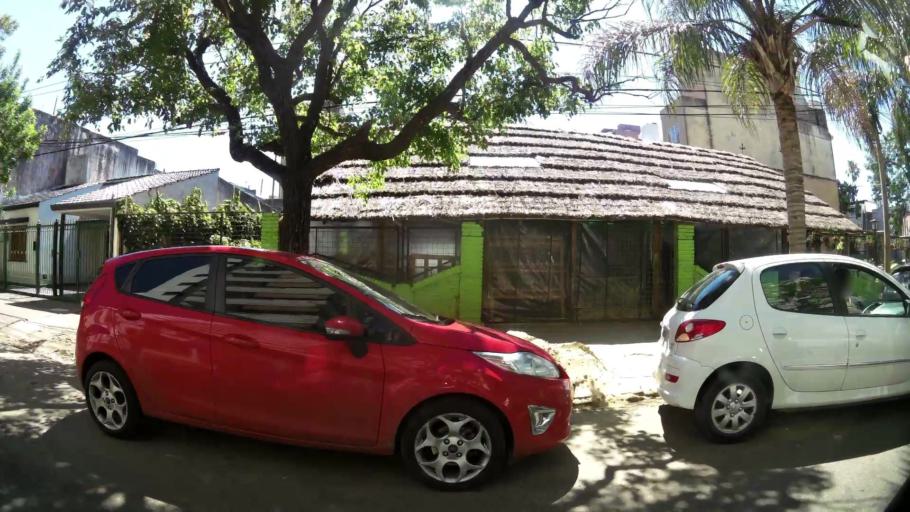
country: AR
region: Santa Fe
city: Santa Fe de la Vera Cruz
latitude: -31.6392
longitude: -60.6882
